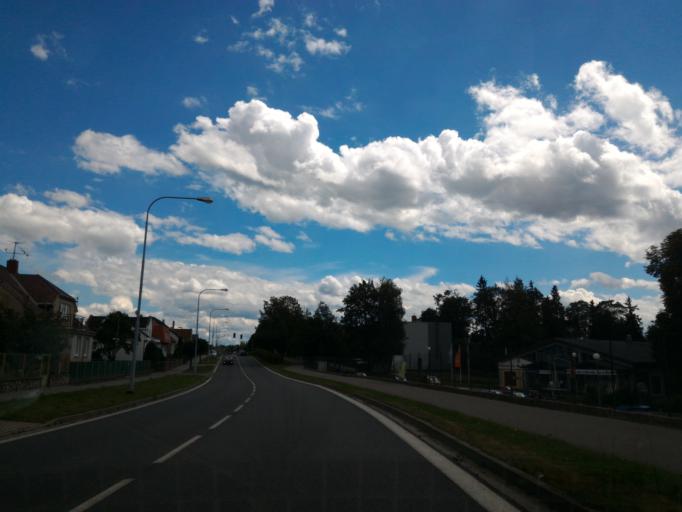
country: CZ
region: Vysocina
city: Zd'ar nad Sazavou Druhy
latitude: 49.5767
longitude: 15.9385
